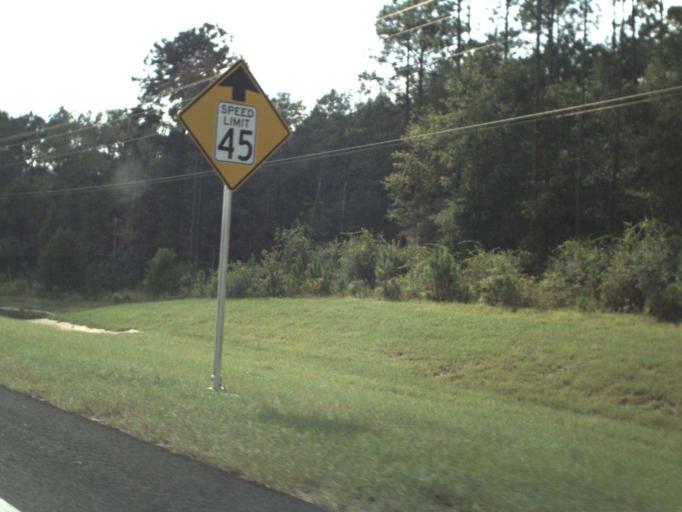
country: US
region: Florida
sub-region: Bay County
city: Laguna Beach
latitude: 30.4545
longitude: -85.8728
